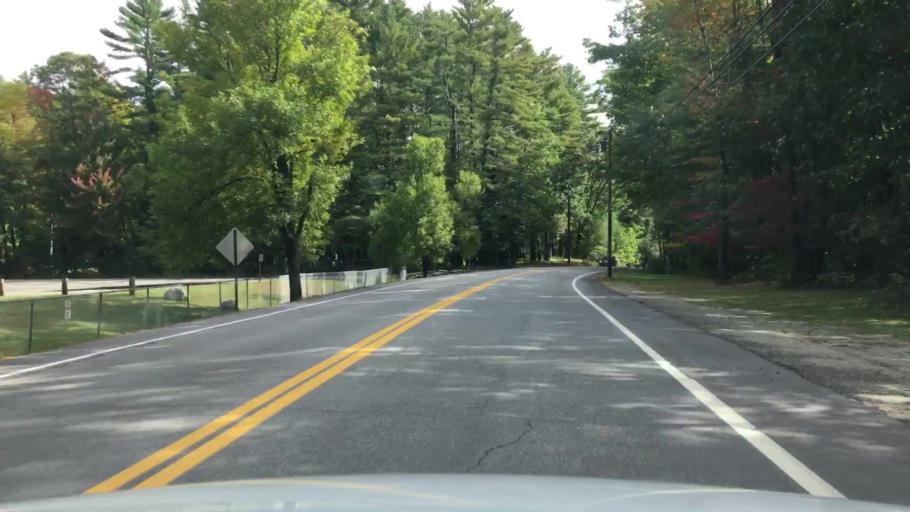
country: US
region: Maine
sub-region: Cumberland County
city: Brunswick
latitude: 43.9231
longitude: -69.9388
